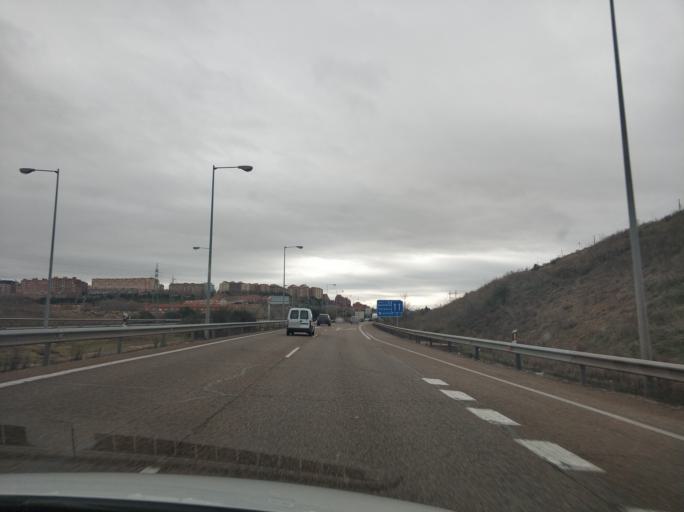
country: ES
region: Castille and Leon
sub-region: Provincia de Valladolid
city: Zaratan
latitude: 41.6483
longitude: -4.7656
